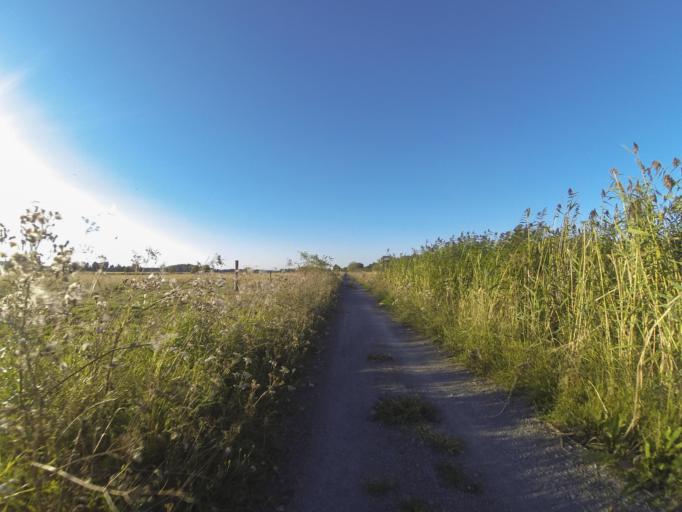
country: SE
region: Vaestmanland
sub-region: Vasteras
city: Vasteras
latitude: 59.5614
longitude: 16.6492
